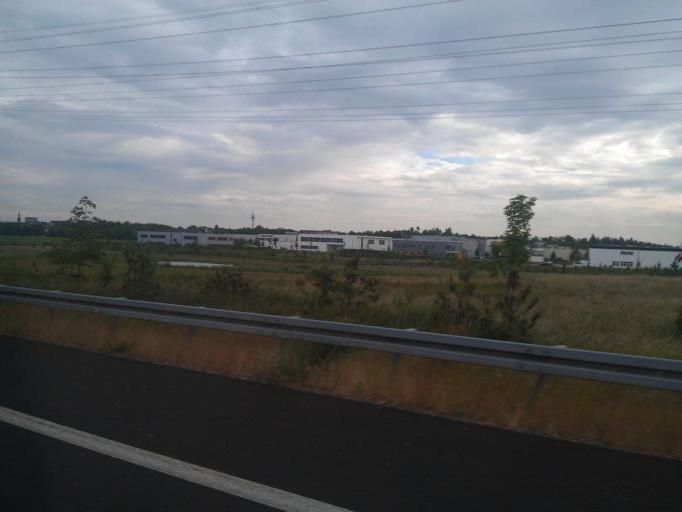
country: DE
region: North Rhine-Westphalia
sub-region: Regierungsbezirk Dusseldorf
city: Dusseldorf
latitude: 51.1643
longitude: 6.7425
